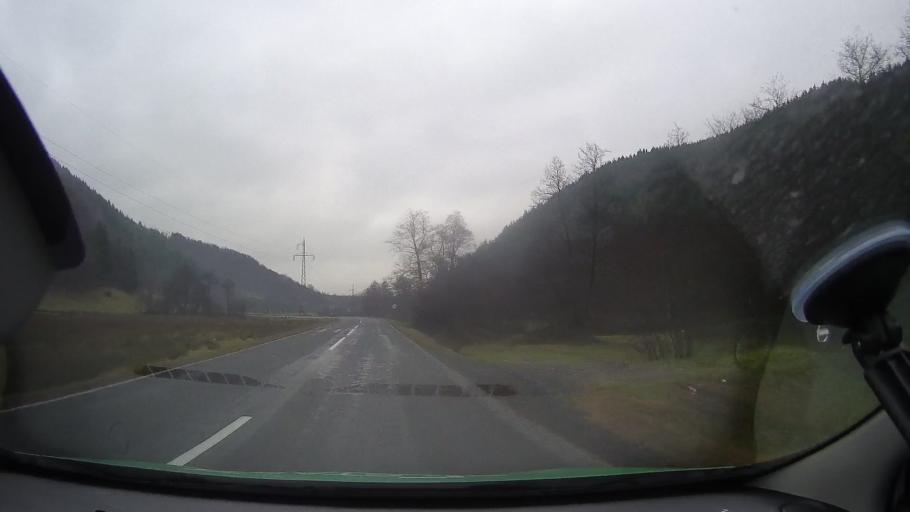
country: RO
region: Arad
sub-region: Comuna Varfurile
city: Varfurile
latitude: 46.3177
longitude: 22.4733
